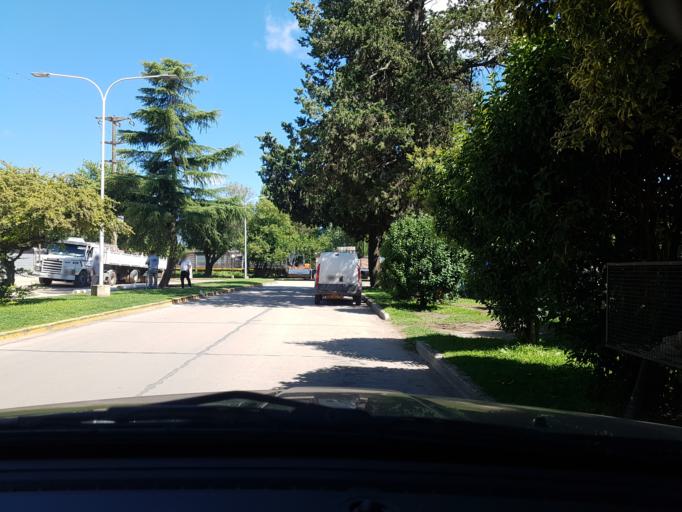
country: AR
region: Cordoba
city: General Cabrera
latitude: -32.7566
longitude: -63.7947
